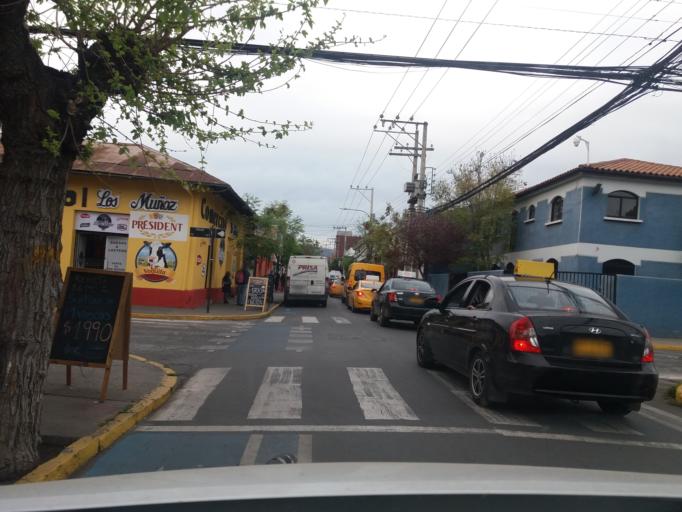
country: CL
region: Valparaiso
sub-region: Provincia de San Felipe
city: San Felipe
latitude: -32.7527
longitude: -70.7250
